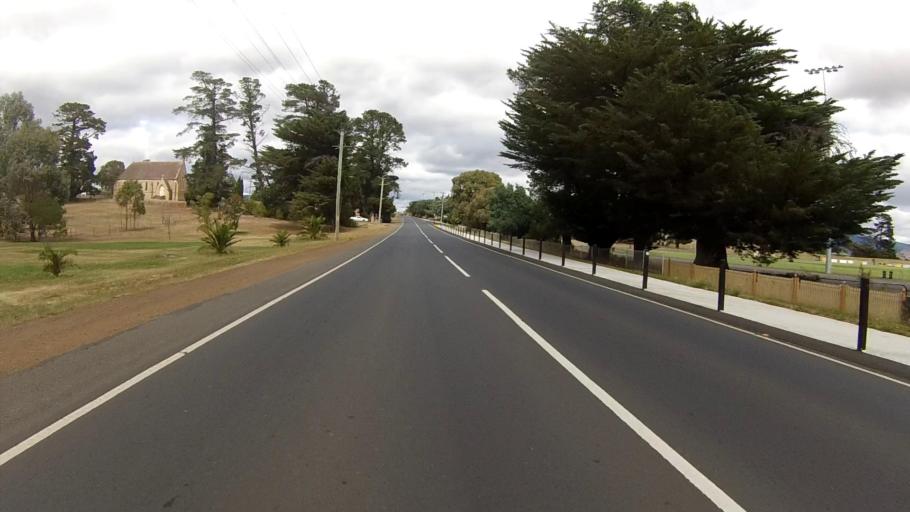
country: AU
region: Tasmania
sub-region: Brighton
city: Bridgewater
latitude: -42.6873
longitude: 147.2637
